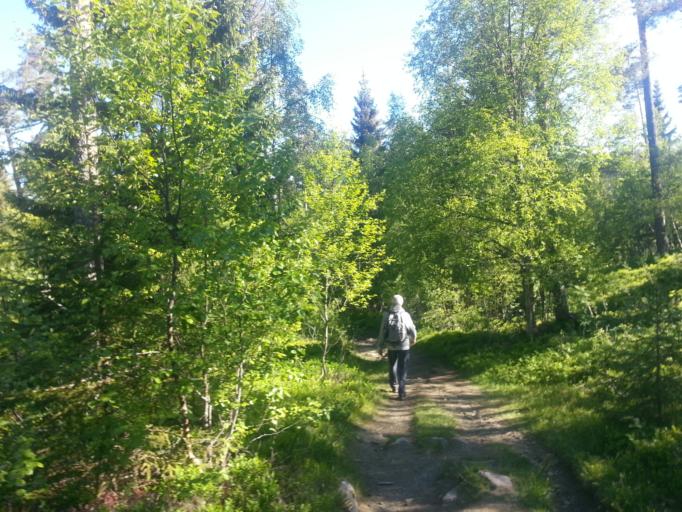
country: NO
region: Sor-Trondelag
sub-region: Trondheim
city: Trondheim
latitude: 63.4221
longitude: 10.3307
